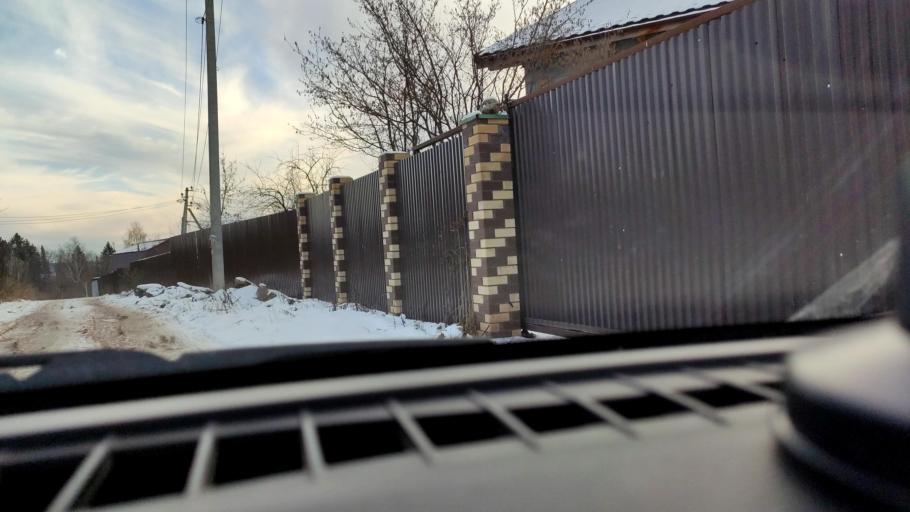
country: RU
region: Perm
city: Froly
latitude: 57.9456
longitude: 56.2801
